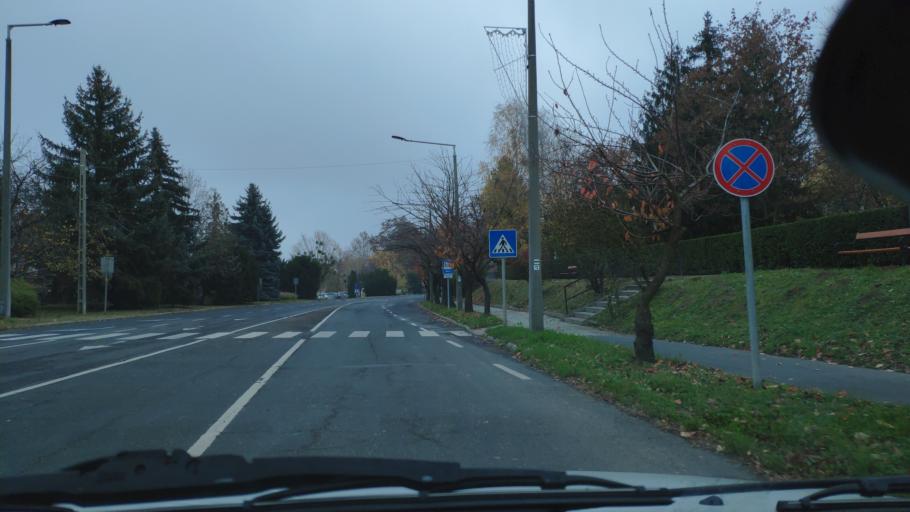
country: HU
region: Zala
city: Zalakomar
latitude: 46.5519
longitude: 17.1225
